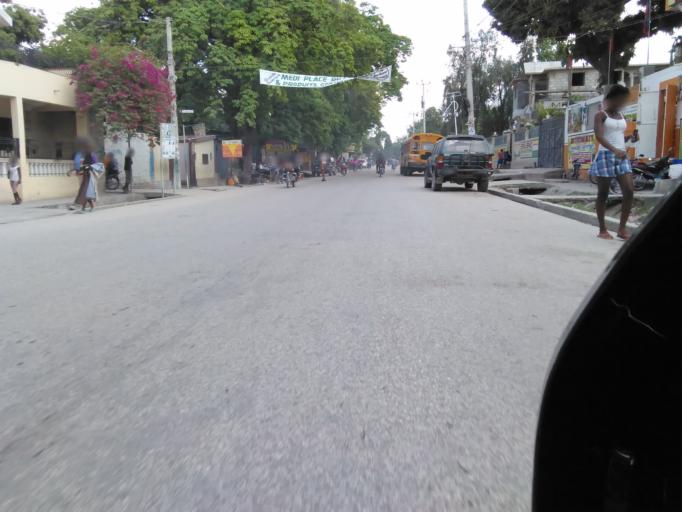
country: HT
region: Artibonite
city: Saint-Marc
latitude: 19.1064
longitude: -72.6956
